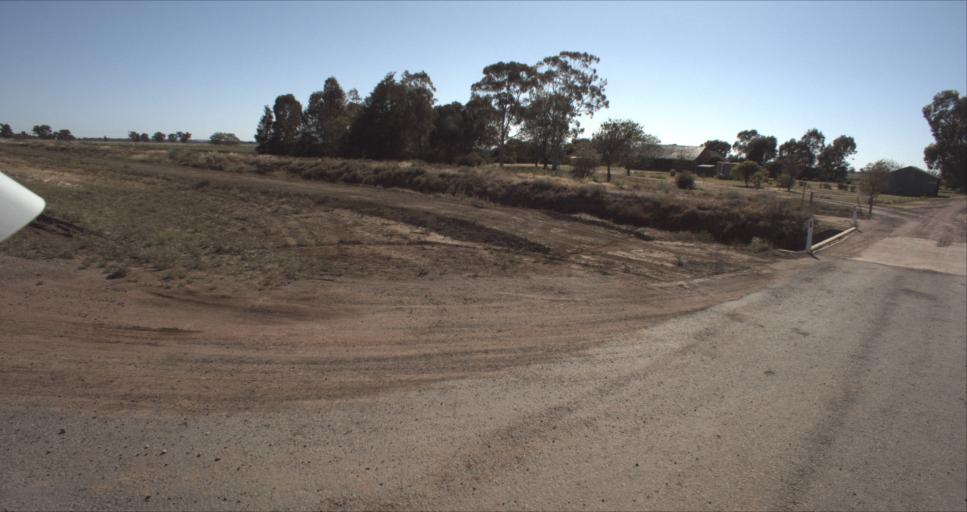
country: AU
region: New South Wales
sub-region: Leeton
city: Leeton
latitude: -34.5834
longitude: 146.3084
